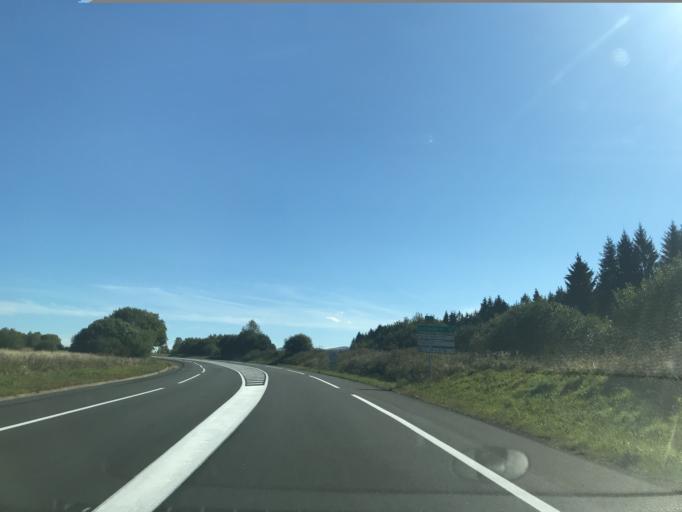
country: FR
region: Auvergne
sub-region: Departement du Puy-de-Dome
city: Saint-Sauves-d'Auvergne
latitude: 45.6548
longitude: 2.6939
